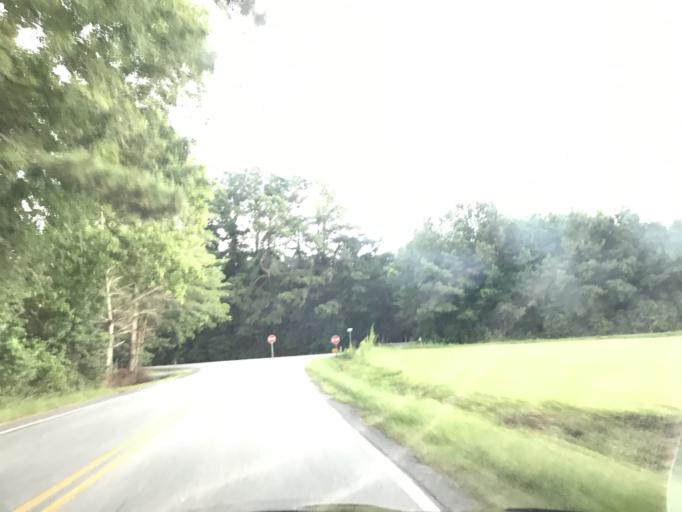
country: US
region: North Carolina
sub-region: Johnston County
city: Wilsons Mills
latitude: 35.5416
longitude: -78.4067
